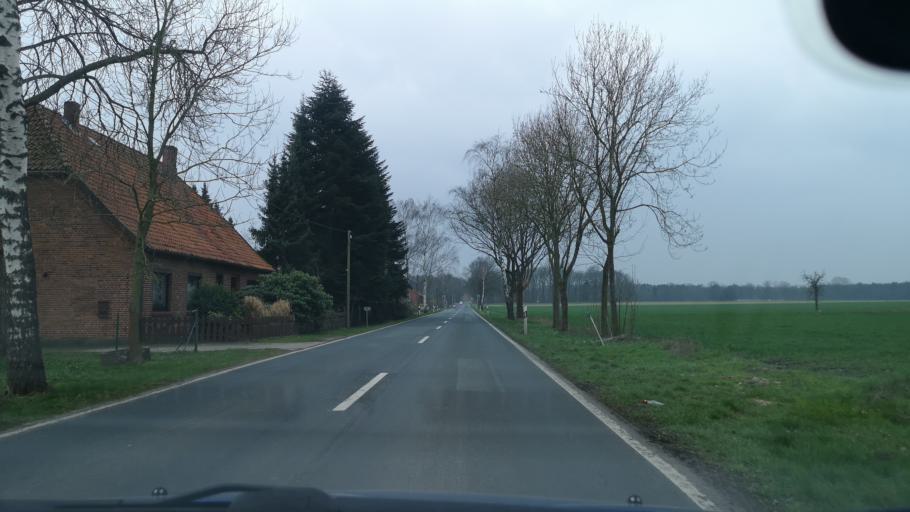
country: DE
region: Lower Saxony
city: Neustadt am Rubenberge
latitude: 52.5425
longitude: 9.4030
